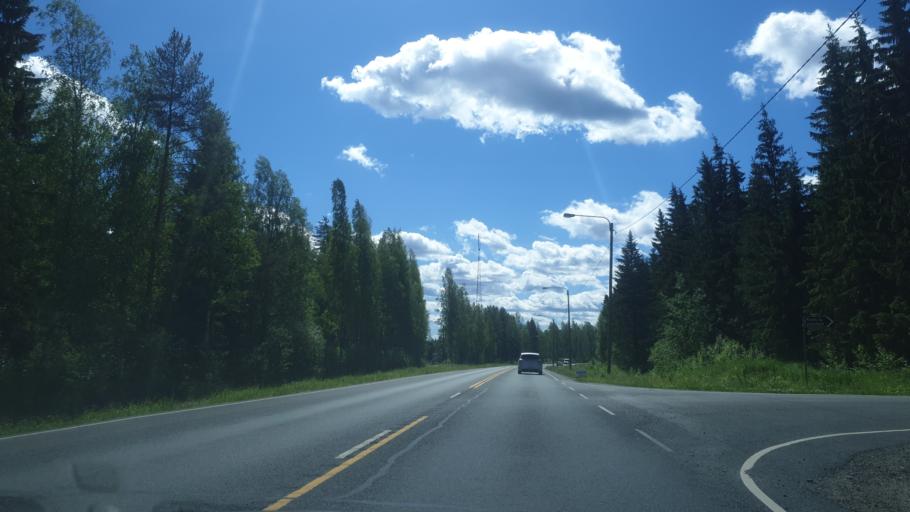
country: FI
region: Northern Savo
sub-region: Varkaus
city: Leppaevirta
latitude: 62.5857
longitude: 27.6052
